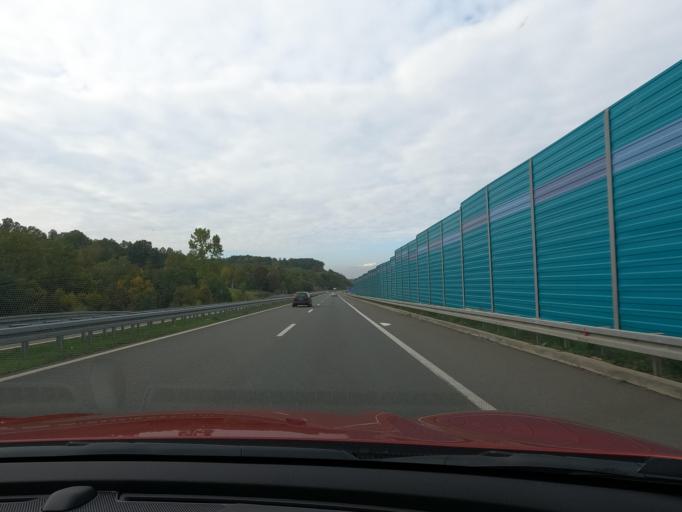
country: RS
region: Central Serbia
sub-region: Moravicki Okrug
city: Gornji Milanovac
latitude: 44.1279
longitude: 20.3643
